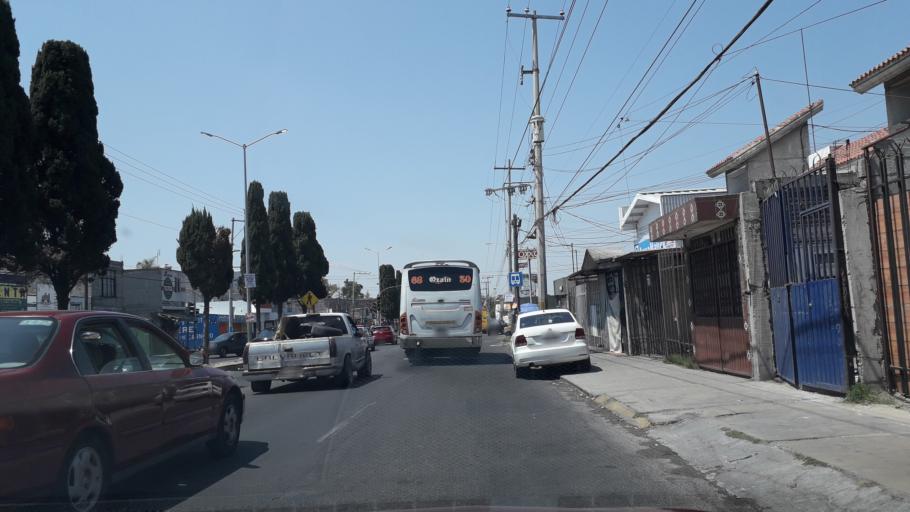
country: MX
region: Puebla
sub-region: Amozoc
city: Casa Blanca
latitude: 19.0657
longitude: -98.1212
